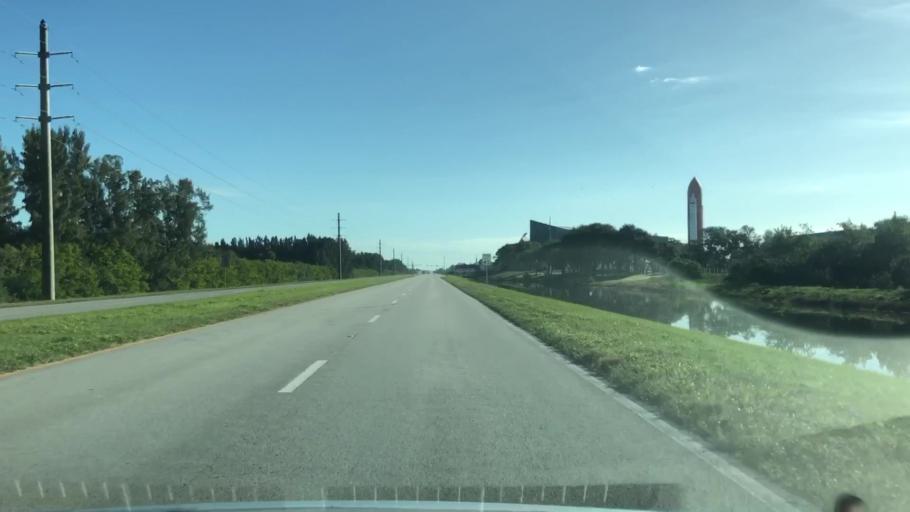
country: US
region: Florida
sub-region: Brevard County
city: Merritt Island
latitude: 28.5264
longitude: -80.6857
